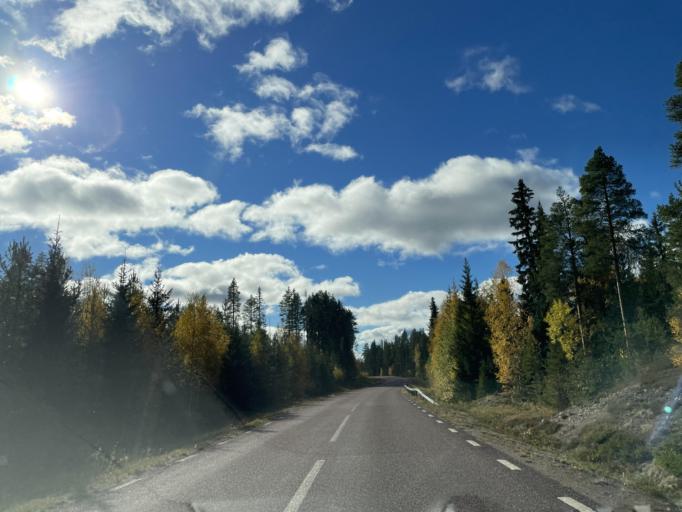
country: NO
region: Hedmark
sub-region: Trysil
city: Innbygda
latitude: 61.5052
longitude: 13.0774
